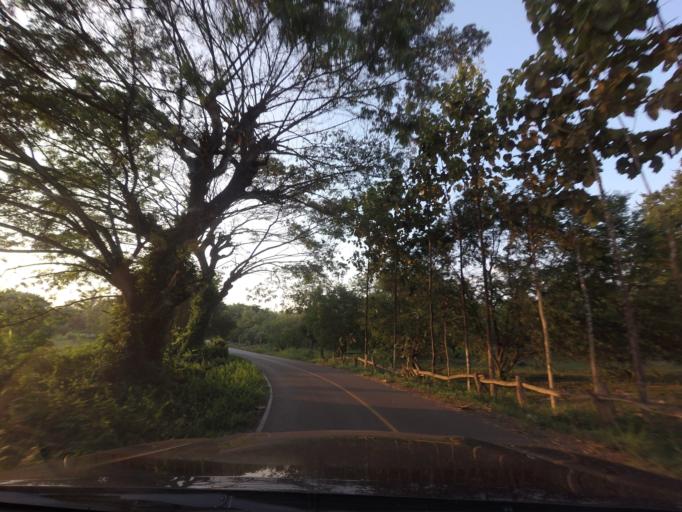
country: TH
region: Nan
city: Na Noi
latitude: 18.3158
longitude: 100.7313
